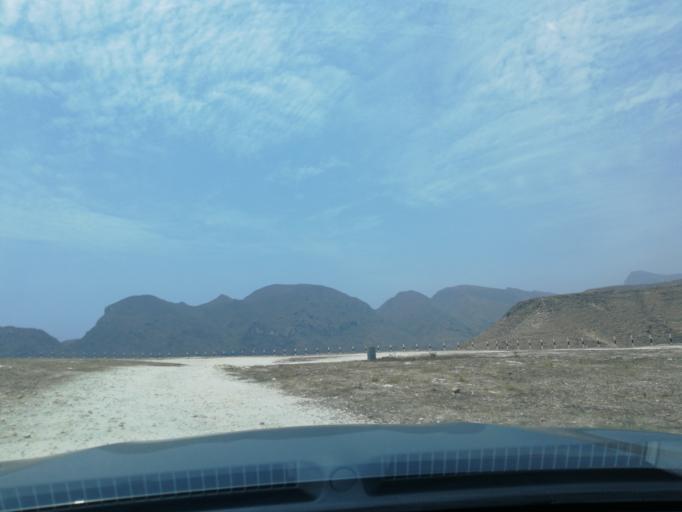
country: OM
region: Zufar
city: Salalah
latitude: 16.8803
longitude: 53.7462
